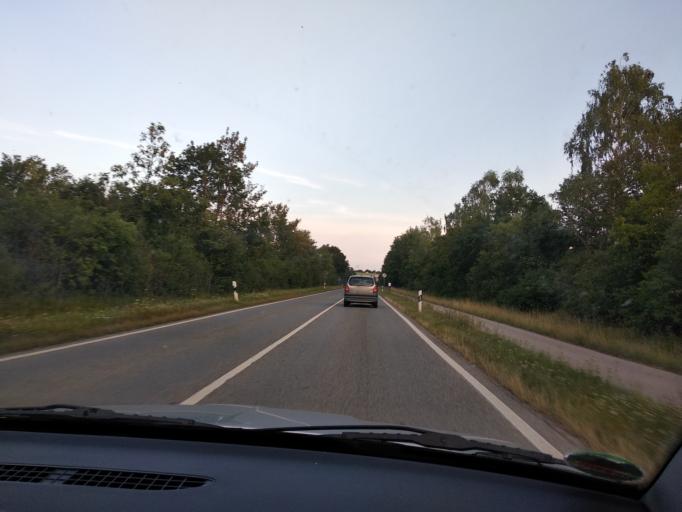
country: DE
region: Bavaria
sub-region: Upper Bavaria
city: Feldkirchen
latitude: 48.1417
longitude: 11.7549
